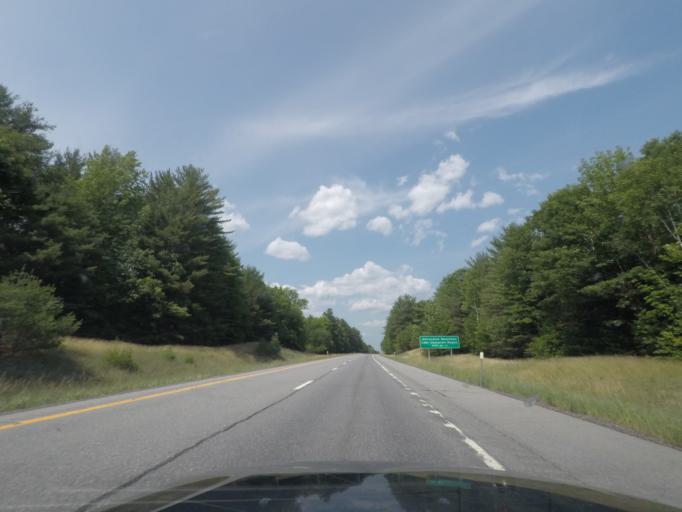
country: US
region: New York
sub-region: Essex County
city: Ticonderoga
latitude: 43.8497
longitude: -73.7649
